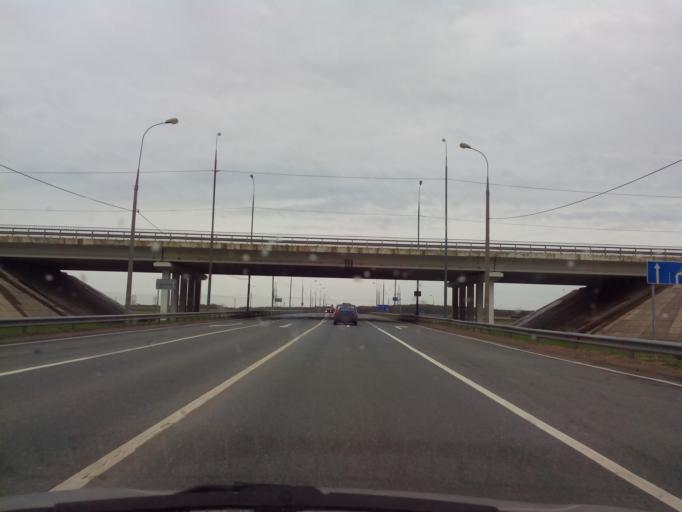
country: RU
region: Moskovskaya
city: Kashira
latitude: 54.7773
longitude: 38.1412
